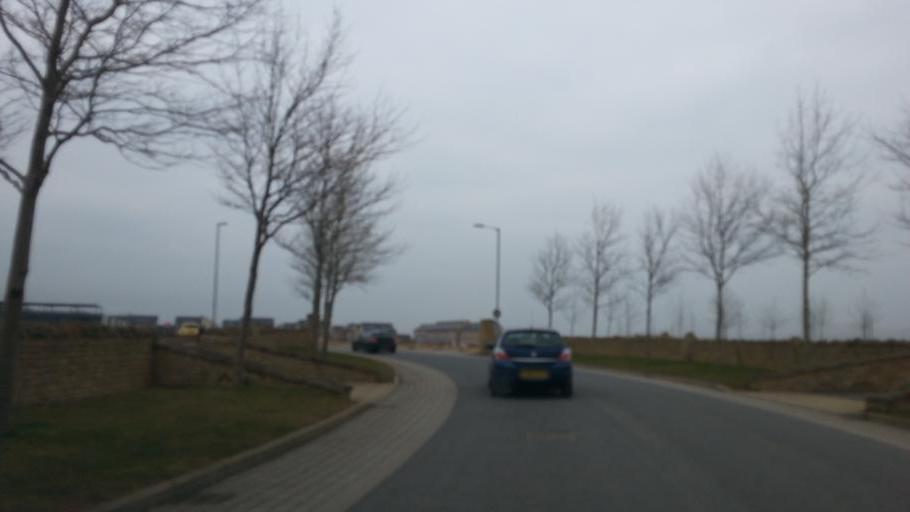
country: GB
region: England
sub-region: Northamptonshire
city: Corby
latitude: 52.5065
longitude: -0.6387
